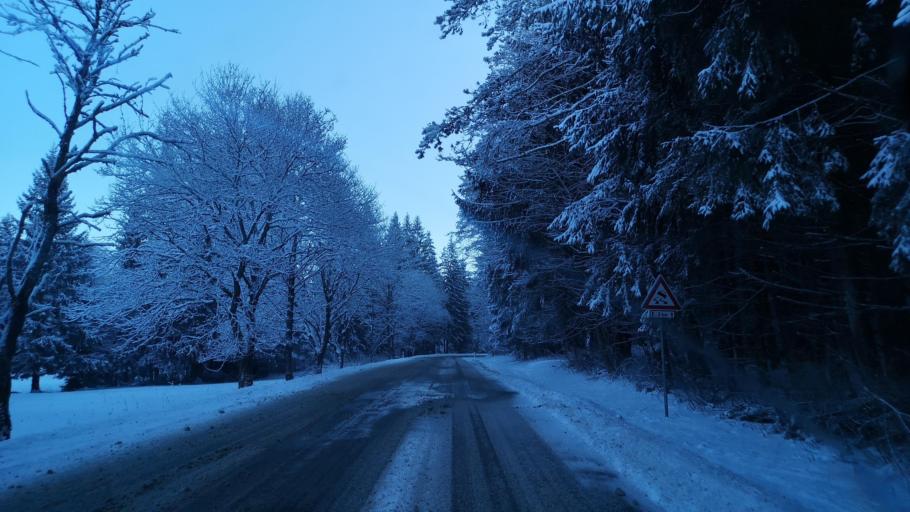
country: SK
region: Banskobystricky
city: Revuca
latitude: 48.8294
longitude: 20.1087
